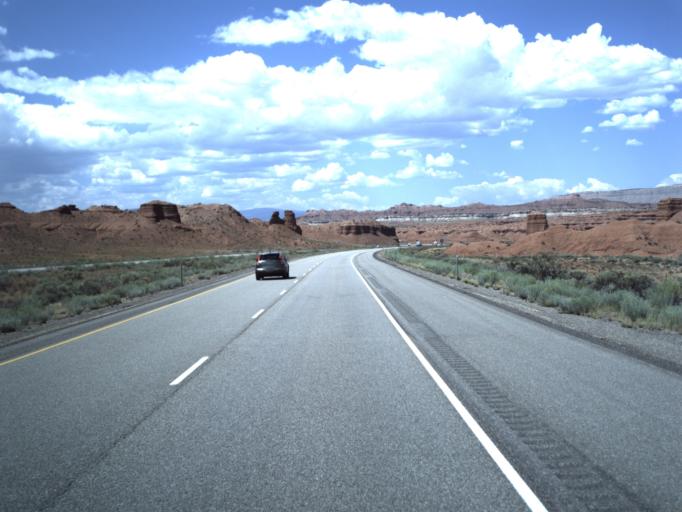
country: US
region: Utah
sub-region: Emery County
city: Ferron
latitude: 38.8461
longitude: -111.0431
